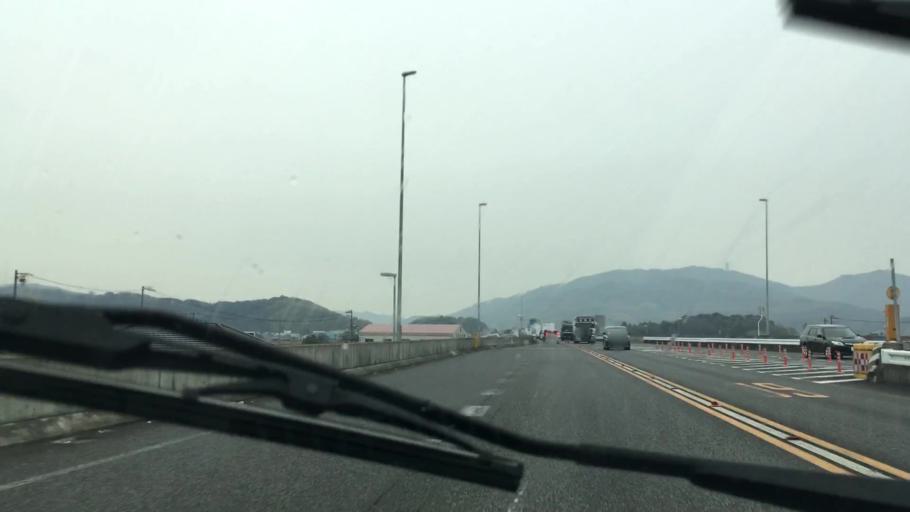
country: JP
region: Aichi
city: Nishio
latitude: 34.8658
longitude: 137.0929
